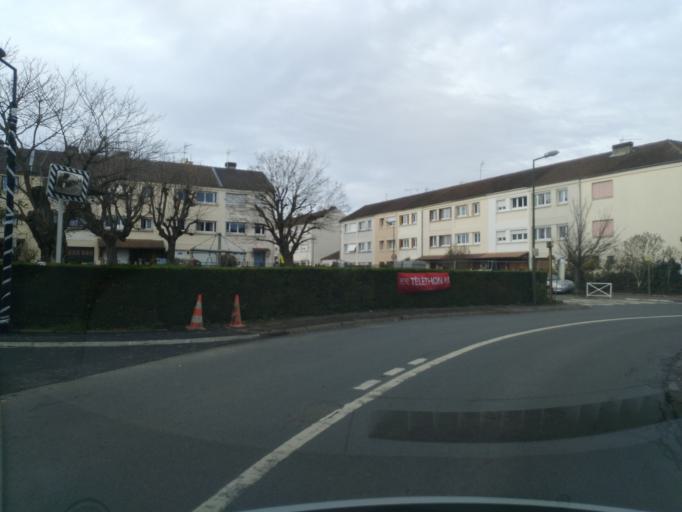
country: FR
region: Ile-de-France
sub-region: Departement des Yvelines
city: Villepreux
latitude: 48.8239
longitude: 1.9996
